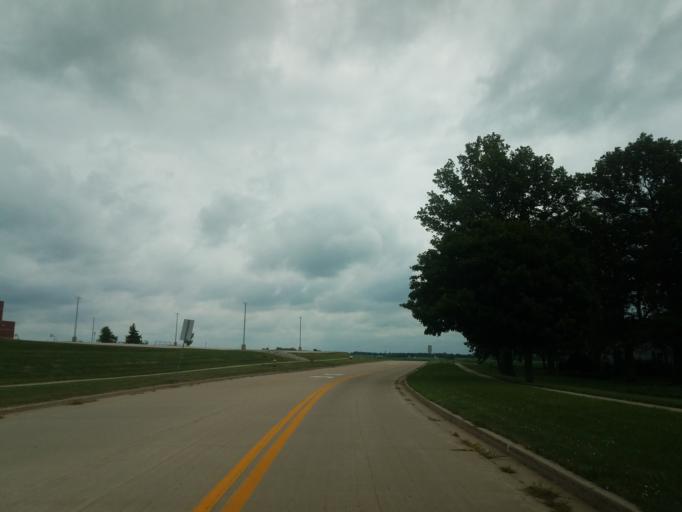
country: US
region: Illinois
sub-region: McLean County
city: Twin Grove
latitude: 40.4369
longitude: -89.0534
